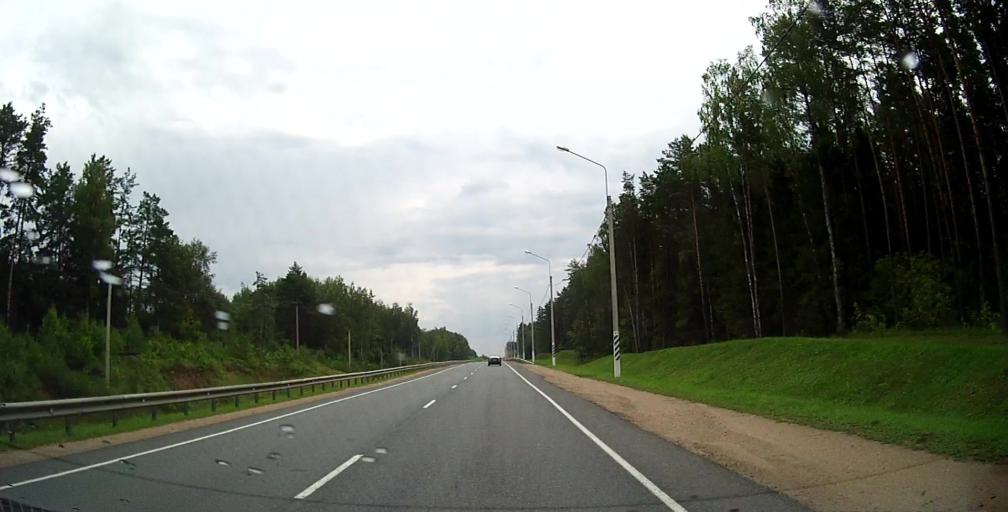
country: RU
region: Smolensk
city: Katyn'
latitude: 54.7732
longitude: 31.7745
